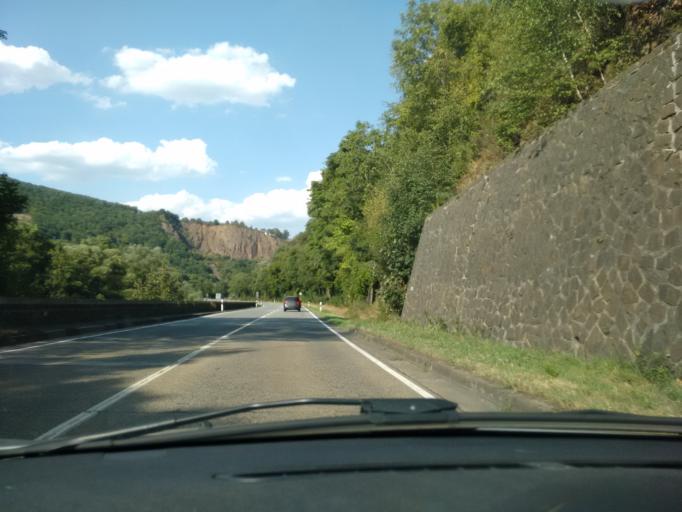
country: DE
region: Rheinland-Pfalz
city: Meckenbach
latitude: 49.7912
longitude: 7.4899
